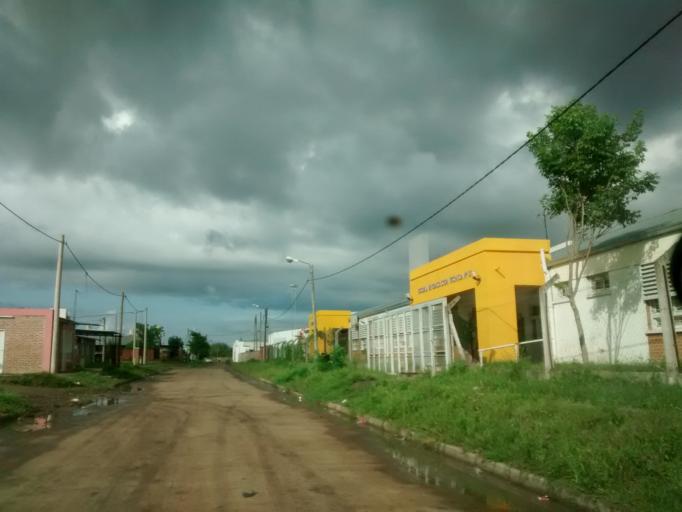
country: AR
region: Chaco
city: Puerto Tirol
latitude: -27.3787
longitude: -59.0919
